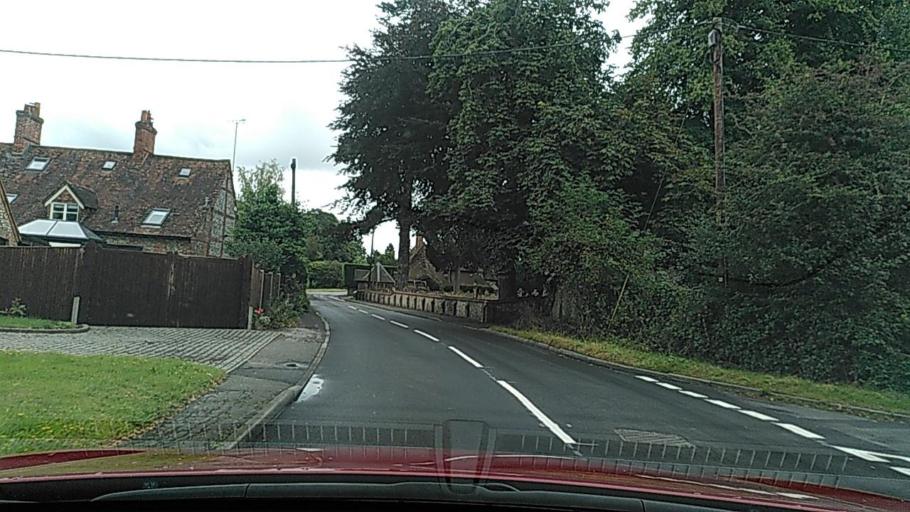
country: GB
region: England
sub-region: Oxfordshire
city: Rotherfield Peppard
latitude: 51.5538
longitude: -0.9914
